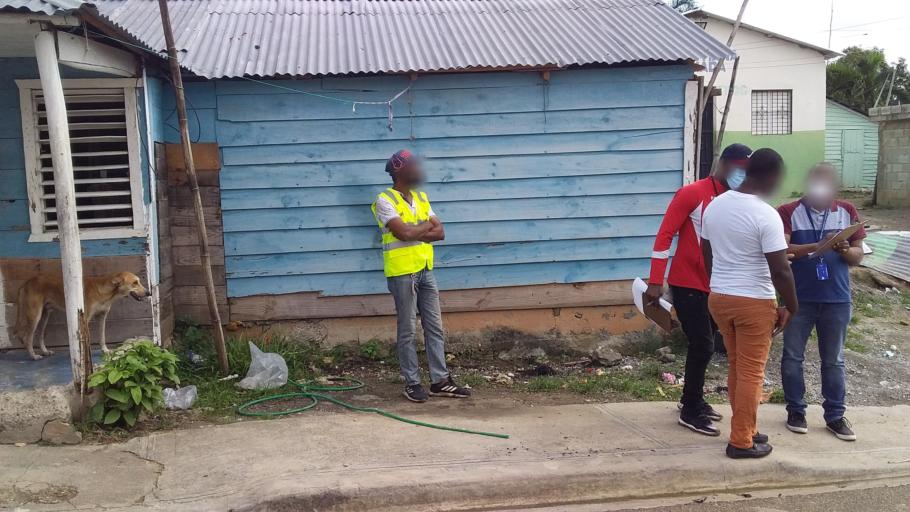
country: DO
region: Santo Domingo
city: Guerra
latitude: 18.5611
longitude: -69.7796
